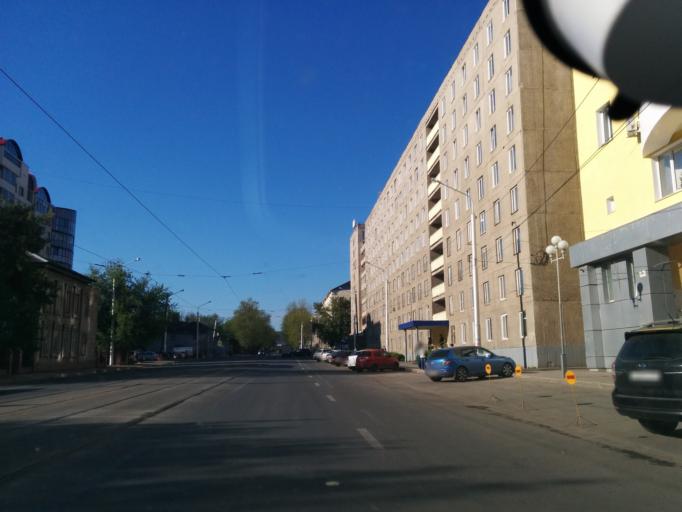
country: RU
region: Bashkortostan
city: Ufa
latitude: 54.7278
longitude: 55.9354
